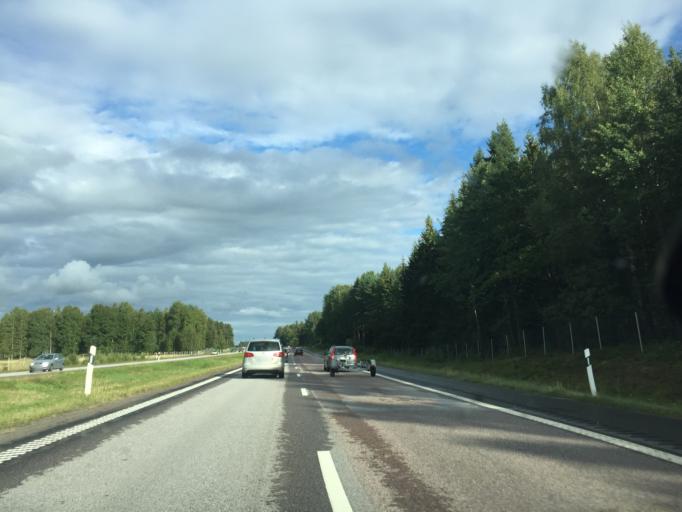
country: SE
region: OErebro
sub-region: Orebro Kommun
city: Hovsta
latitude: 59.3067
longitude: 15.3099
